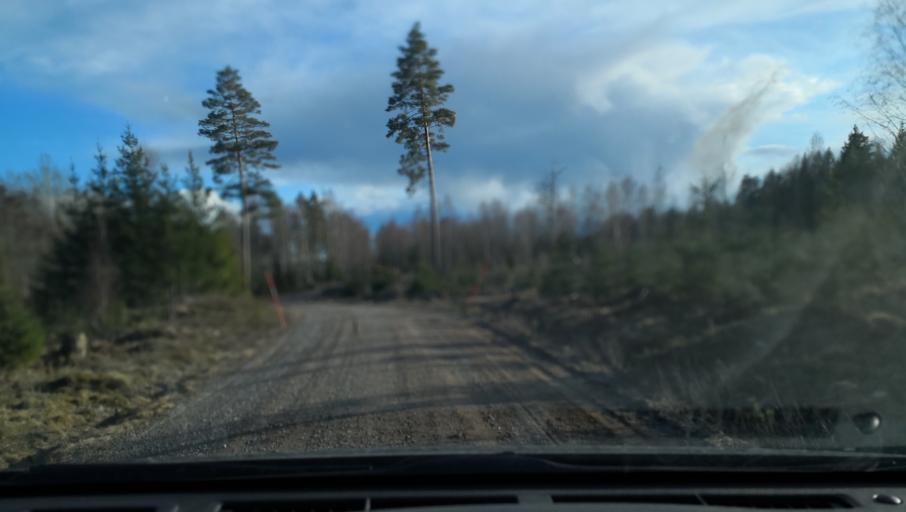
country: SE
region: Vaestmanland
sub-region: Arboga Kommun
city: Arboga
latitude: 59.4319
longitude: 15.7531
